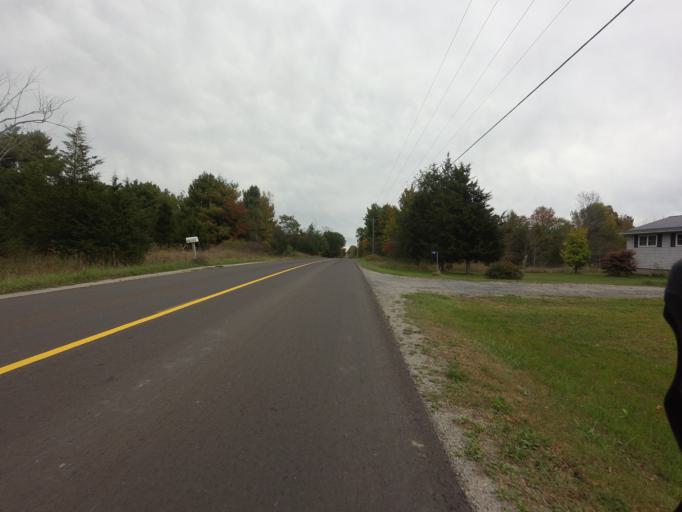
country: CA
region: Ontario
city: Gananoque
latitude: 44.5826
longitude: -76.0475
